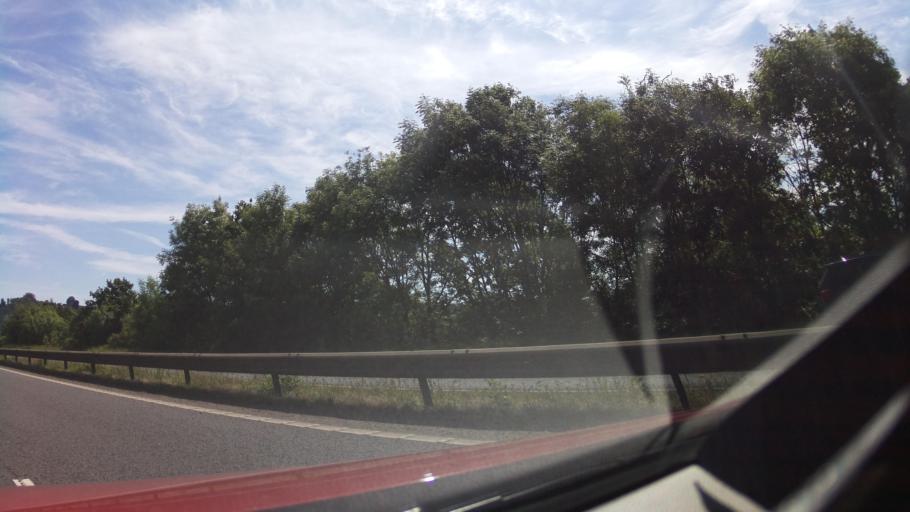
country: GB
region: England
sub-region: Lincolnshire
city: Burton
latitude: 53.2450
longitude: -0.5681
